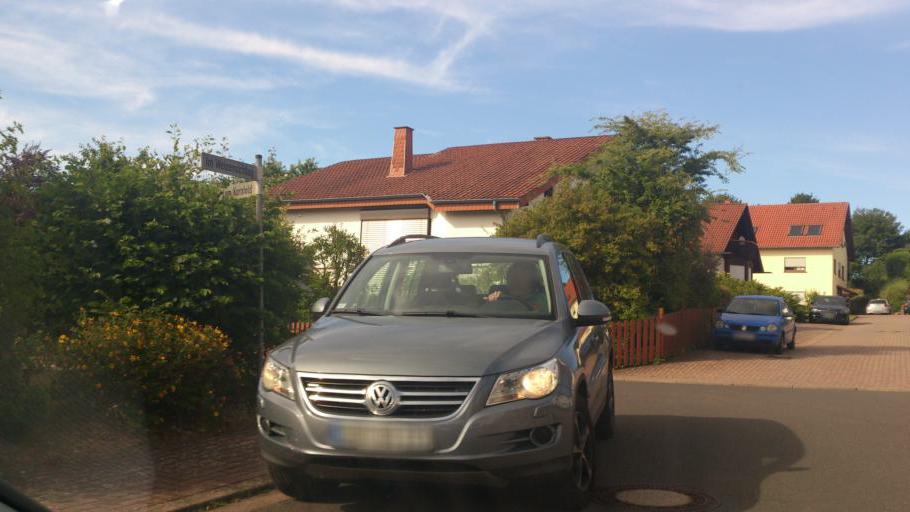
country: DE
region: Saarland
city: Bexbach
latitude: 49.3333
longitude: 7.2679
